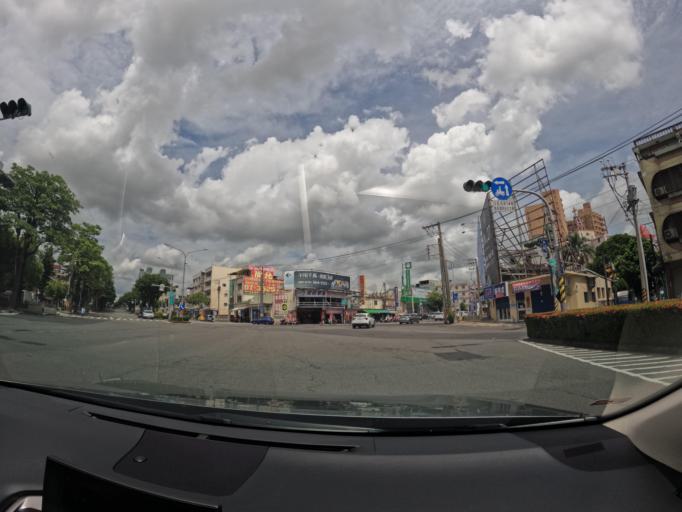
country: TW
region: Kaohsiung
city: Kaohsiung
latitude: 22.7131
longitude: 120.2911
